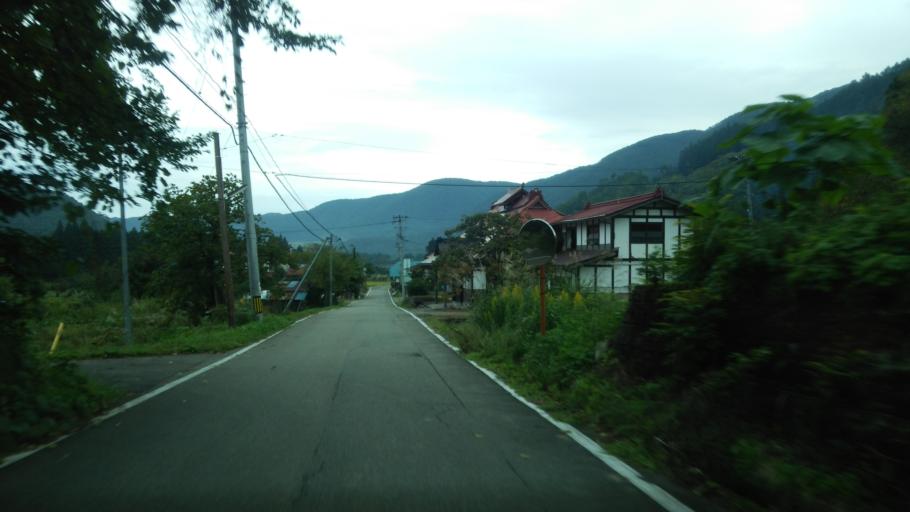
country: JP
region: Fukushima
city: Inawashiro
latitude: 37.3778
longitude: 139.9252
